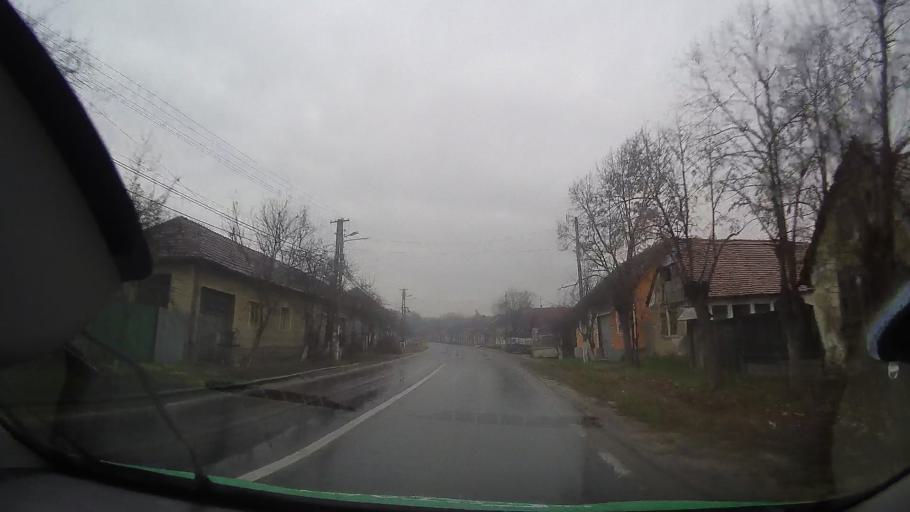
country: RO
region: Bihor
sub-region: Comuna Sambata
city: Sambata
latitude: 46.7986
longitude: 22.2032
